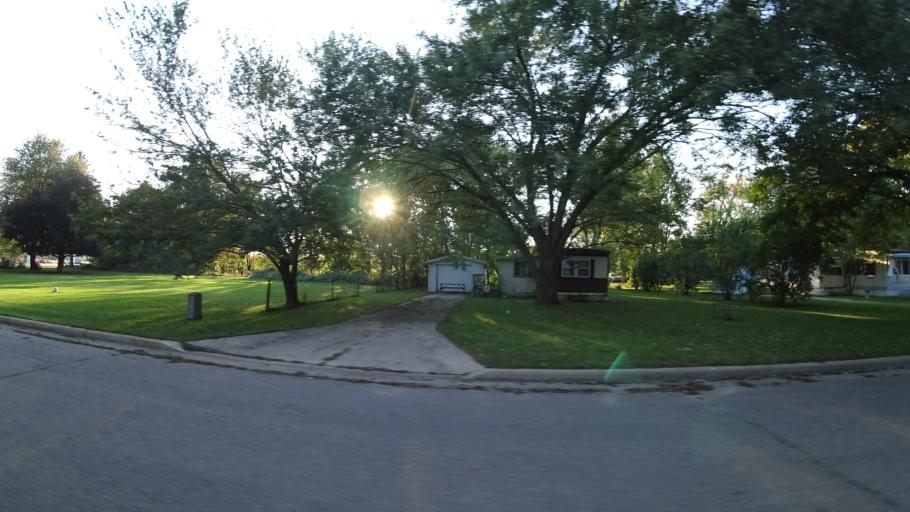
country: US
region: Michigan
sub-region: Saint Joseph County
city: Three Rivers
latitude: 41.9458
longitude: -85.6444
